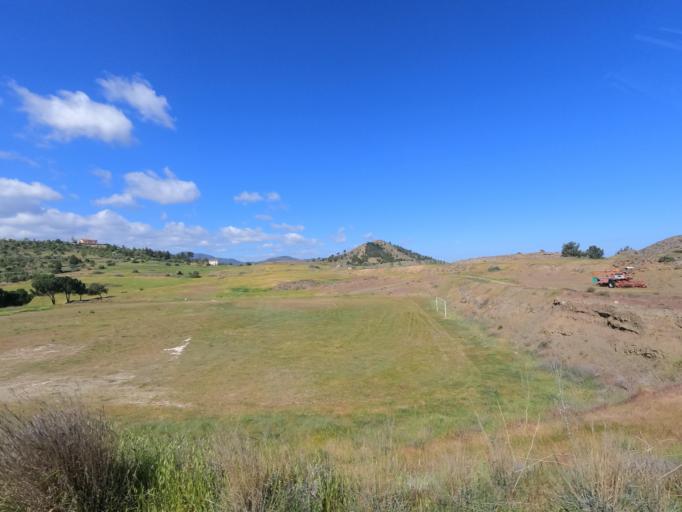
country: CY
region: Lefkosia
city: Peristerona
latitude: 35.0568
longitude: 33.0564
